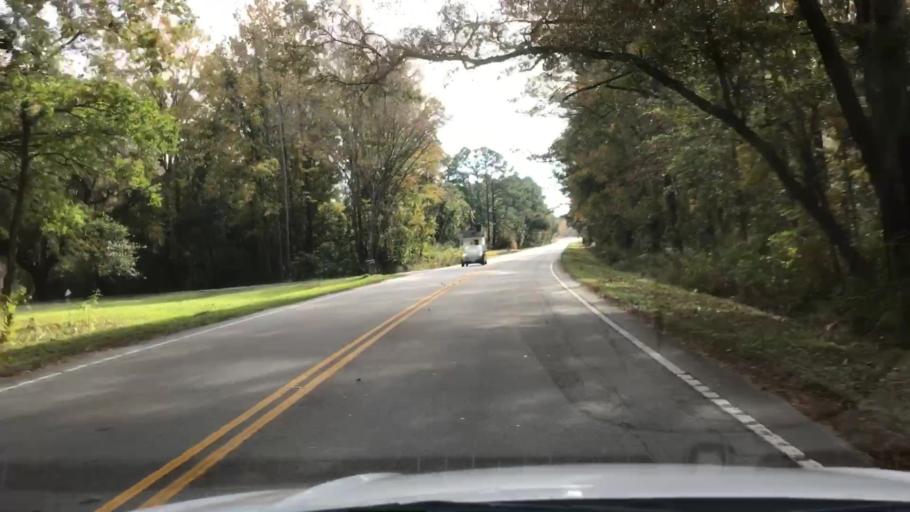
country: US
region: South Carolina
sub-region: Charleston County
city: Ravenel
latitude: 32.7798
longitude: -80.4658
